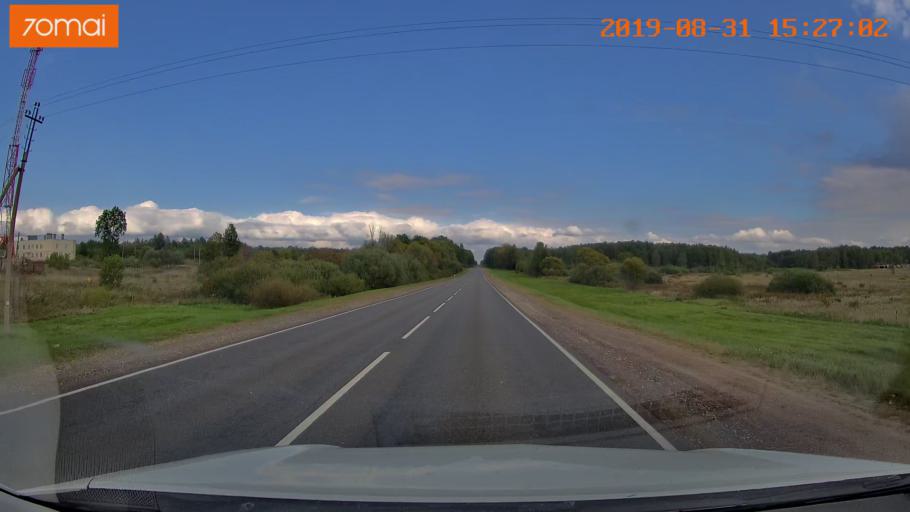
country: RU
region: Kaluga
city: Baryatino
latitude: 54.5534
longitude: 34.5499
